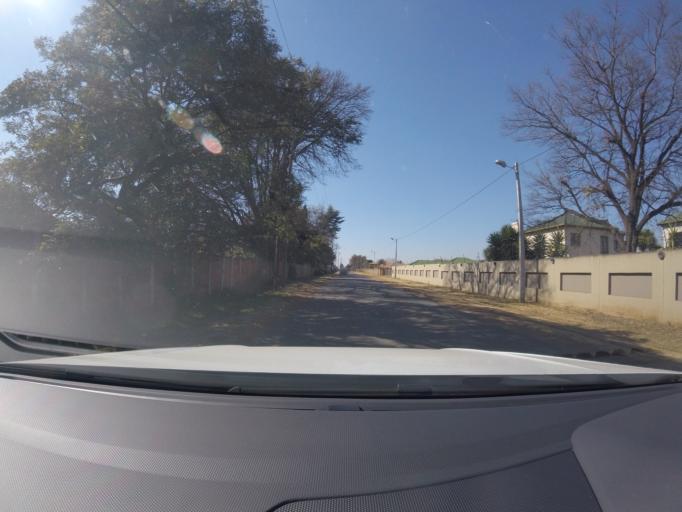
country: ZA
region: Gauteng
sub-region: Ekurhuleni Metropolitan Municipality
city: Benoni
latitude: -26.1233
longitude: 28.2888
